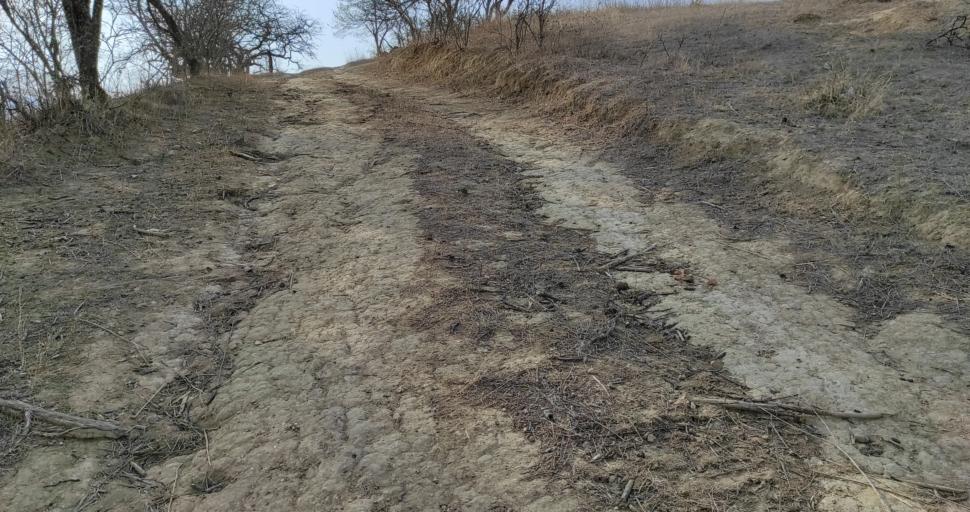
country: EC
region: Loja
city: Catacocha
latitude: -4.0186
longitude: -79.7049
